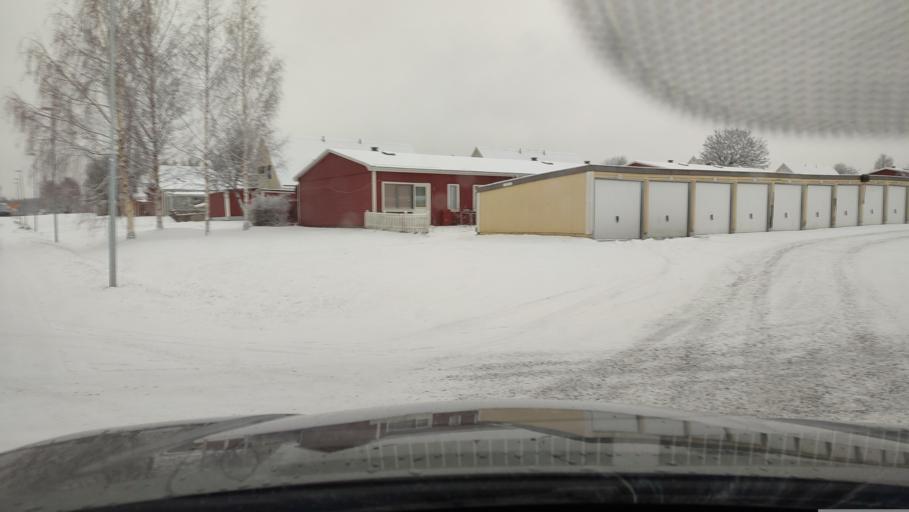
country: SE
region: Vaesterbotten
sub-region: Skelleftea Kommun
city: Skelleftea
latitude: 64.7437
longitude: 20.9828
